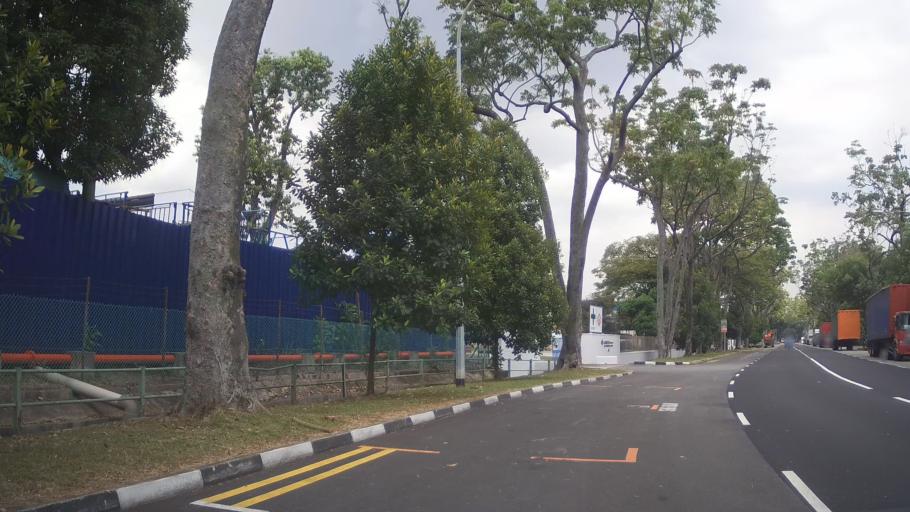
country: MY
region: Johor
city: Johor Bahru
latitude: 1.3143
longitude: 103.6664
